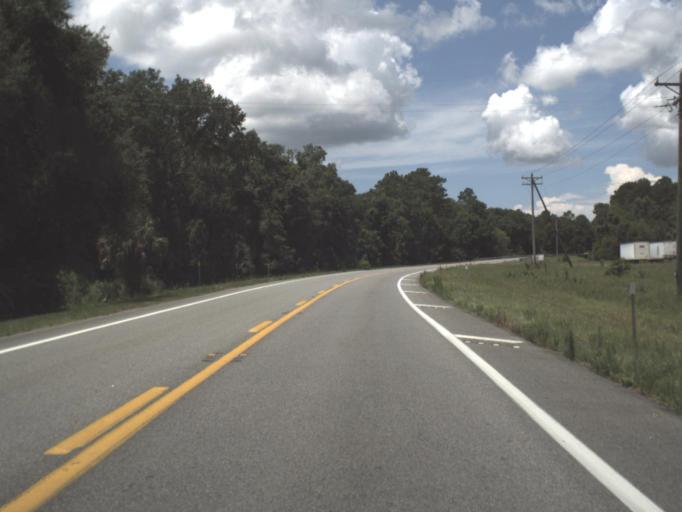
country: US
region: Florida
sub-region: Taylor County
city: Perry
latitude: 30.0848
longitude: -83.6598
